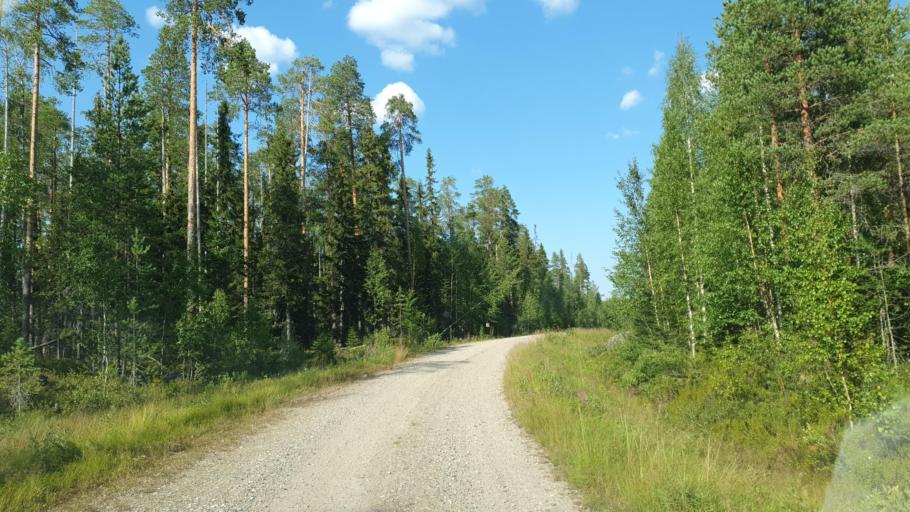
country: FI
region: Kainuu
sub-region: Kehys-Kainuu
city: Kuhmo
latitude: 63.9614
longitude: 29.5357
